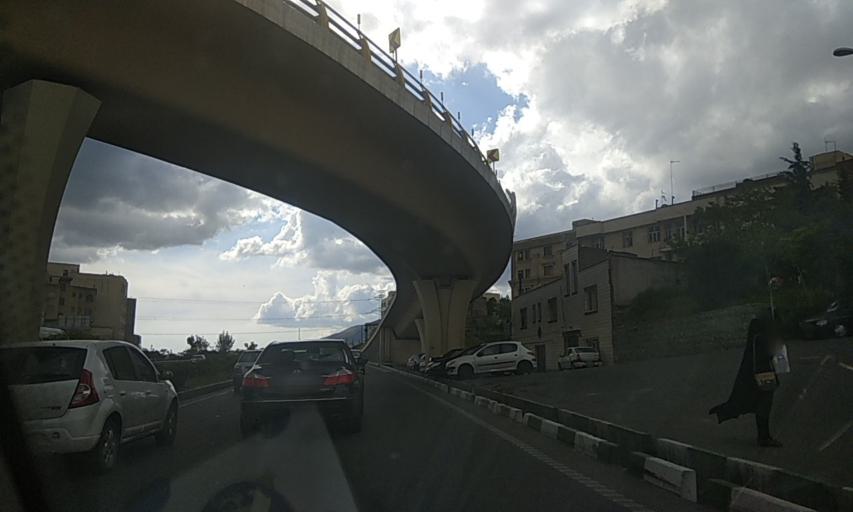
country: IR
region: Tehran
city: Tajrish
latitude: 35.7705
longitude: 51.3235
